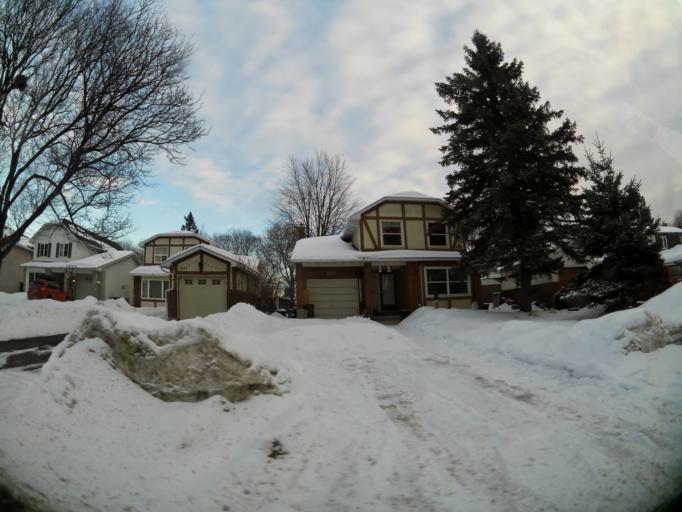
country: CA
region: Quebec
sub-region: Outaouais
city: Gatineau
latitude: 45.4723
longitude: -75.5400
